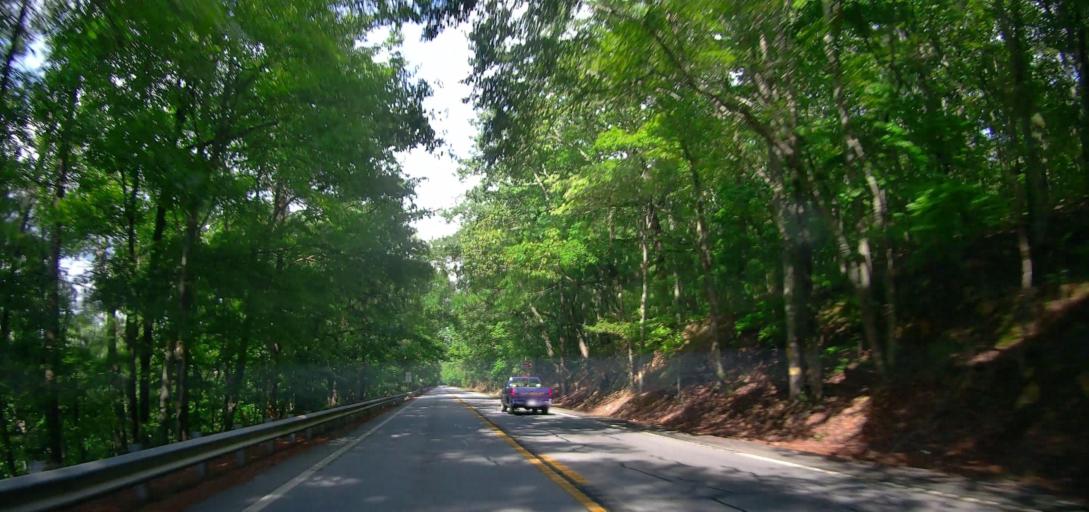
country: US
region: Georgia
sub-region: Harris County
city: Pine Mountain
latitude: 32.8127
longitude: -84.8542
